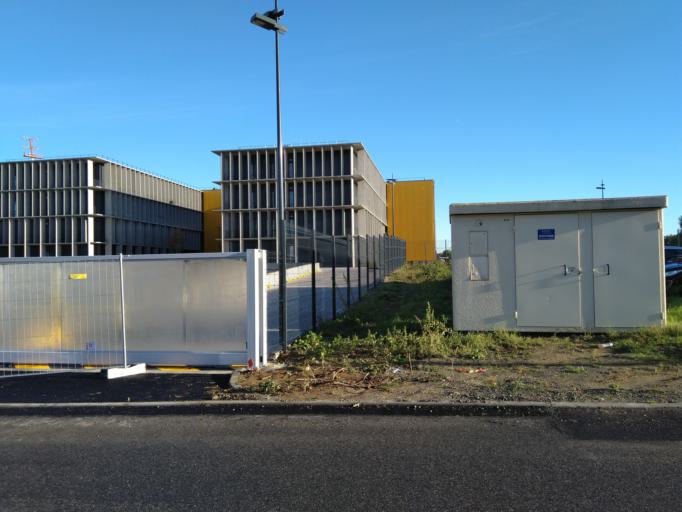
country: FR
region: Midi-Pyrenees
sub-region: Departement de la Haute-Garonne
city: Saint-Orens-de-Gameville
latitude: 43.5418
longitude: 1.5157
